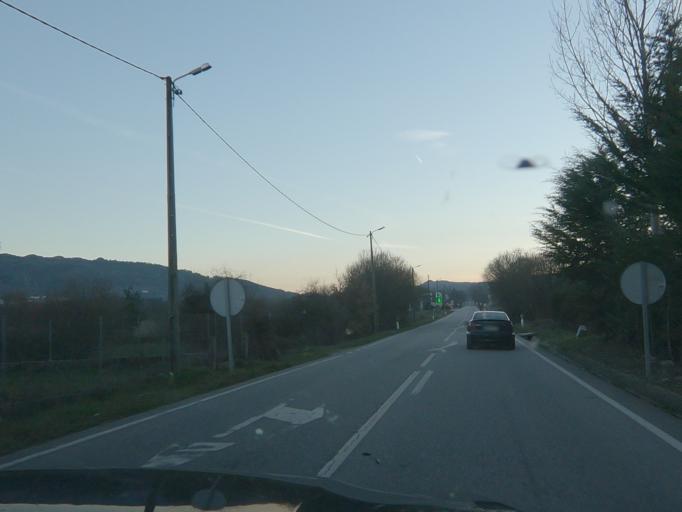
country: PT
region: Vila Real
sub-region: Vila Pouca de Aguiar
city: Vila Pouca de Aguiar
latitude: 41.4372
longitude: -7.6769
